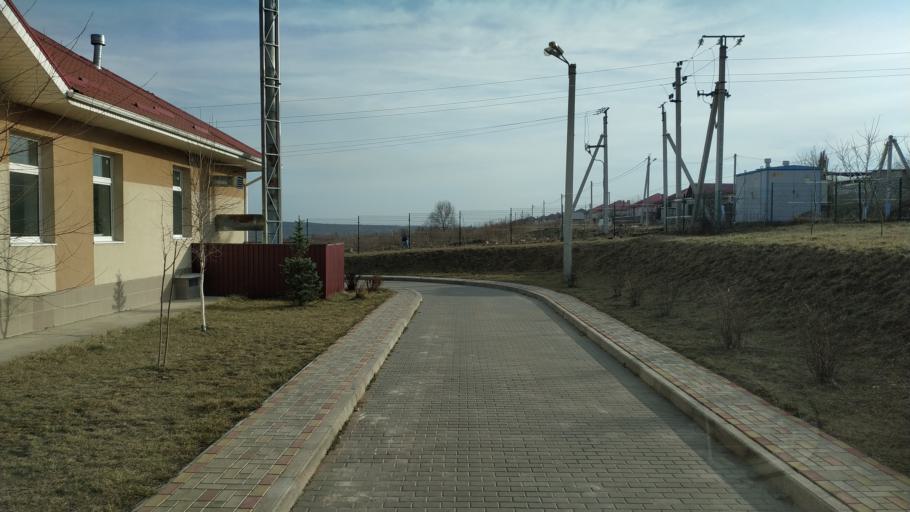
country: RO
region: Vaslui
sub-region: Comuna Dranceni
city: Dranceni
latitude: 46.8387
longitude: 28.1864
